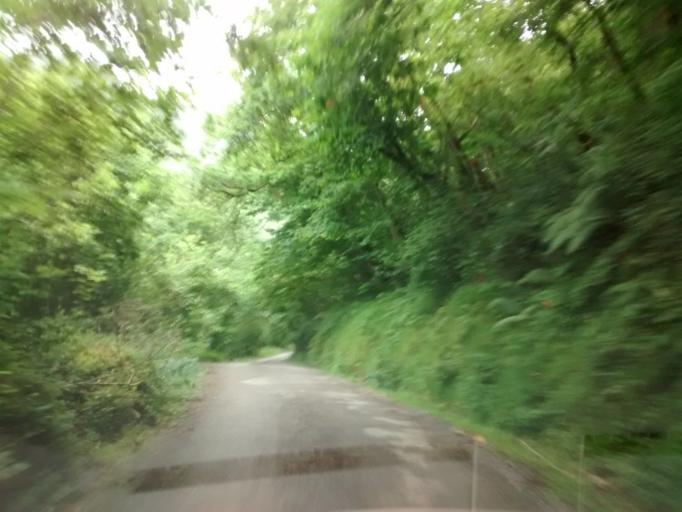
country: ES
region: Asturias
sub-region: Province of Asturias
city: Pilona
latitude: 43.2713
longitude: -5.3436
